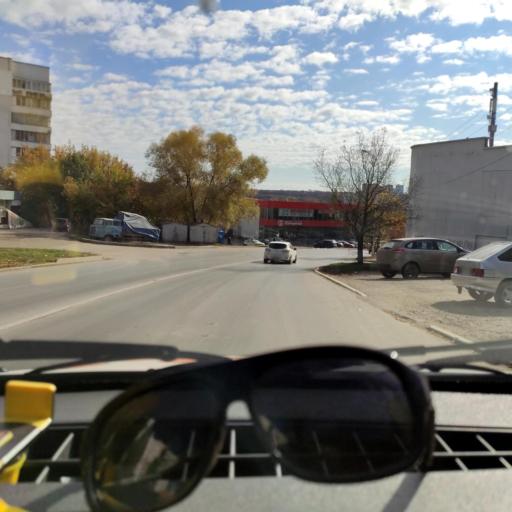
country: RU
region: Bashkortostan
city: Ufa
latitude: 54.7392
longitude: 55.9990
